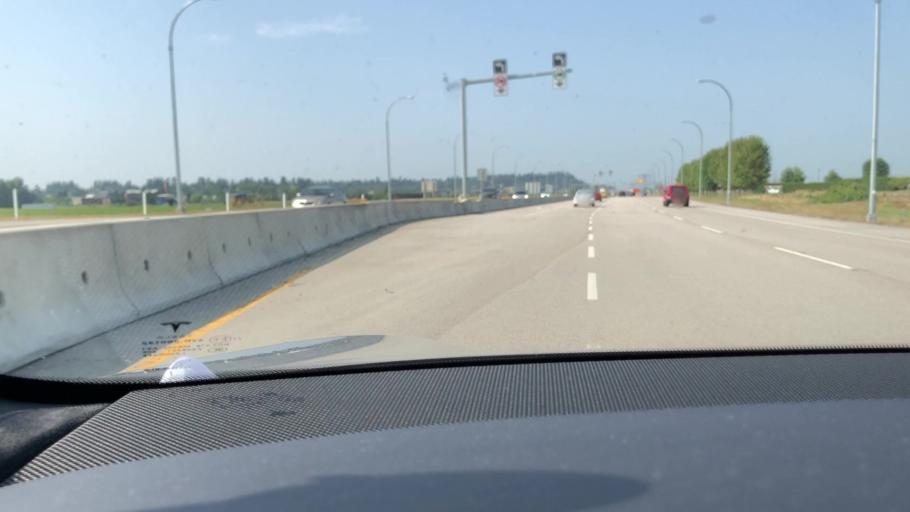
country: CA
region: British Columbia
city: Ladner
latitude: 49.0457
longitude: -123.0628
